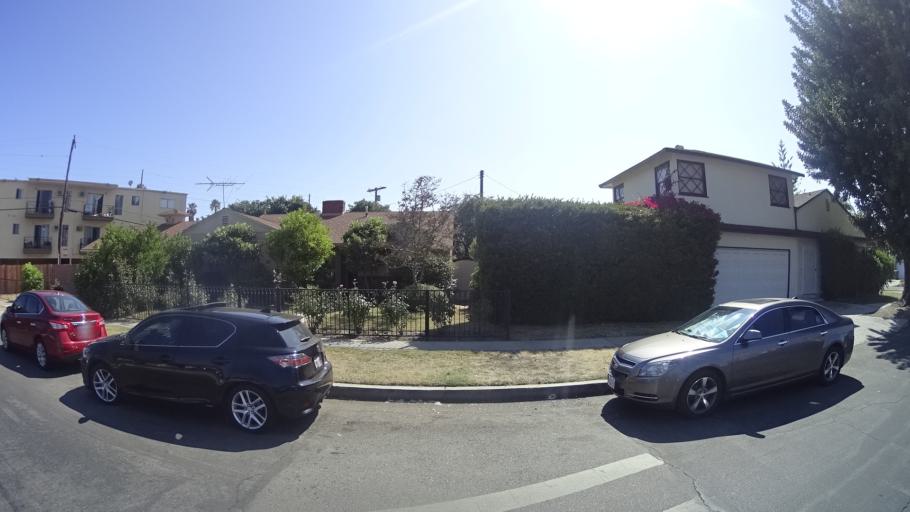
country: US
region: California
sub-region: Los Angeles County
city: Van Nuys
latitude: 34.1948
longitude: -118.4241
